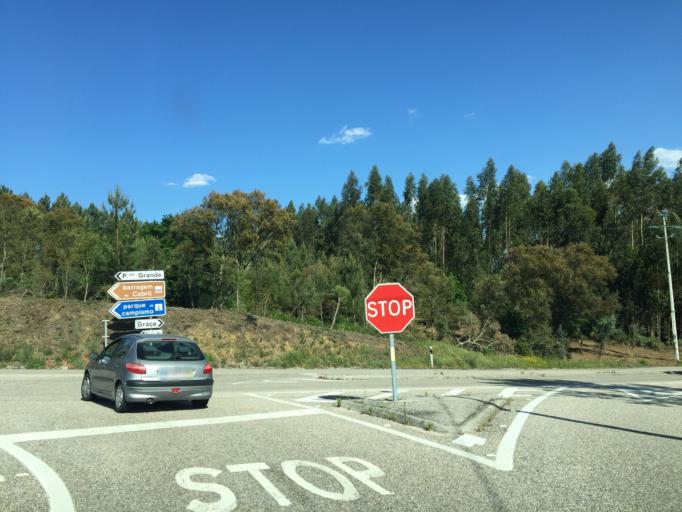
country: PT
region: Leiria
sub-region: Pedrogao Grande
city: Pedrogao Grande
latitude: 39.9091
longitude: -8.1516
